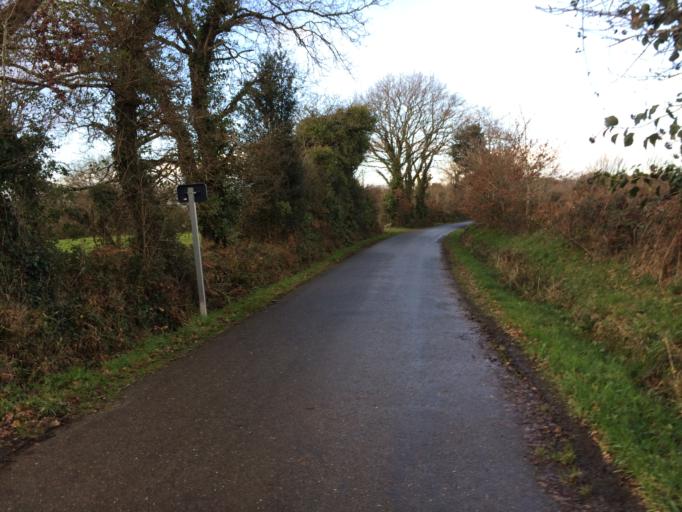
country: FR
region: Brittany
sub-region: Departement du Finistere
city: Hopital-Camfrout
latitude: 48.3296
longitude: -4.2678
